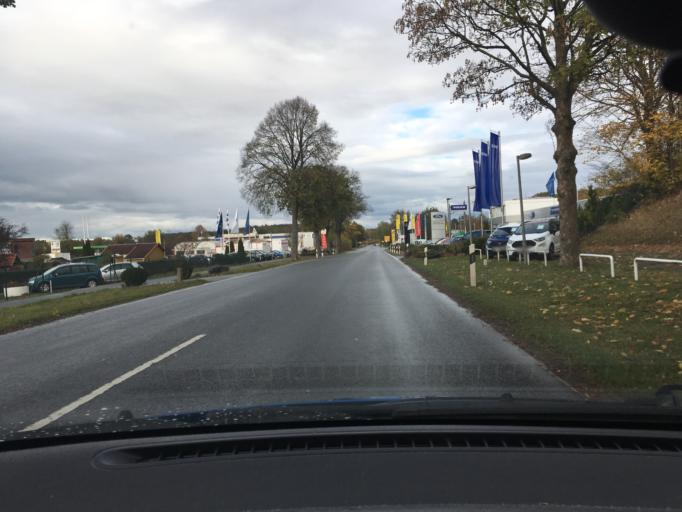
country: DE
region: Schleswig-Holstein
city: Molln
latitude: 53.6382
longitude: 10.6947
